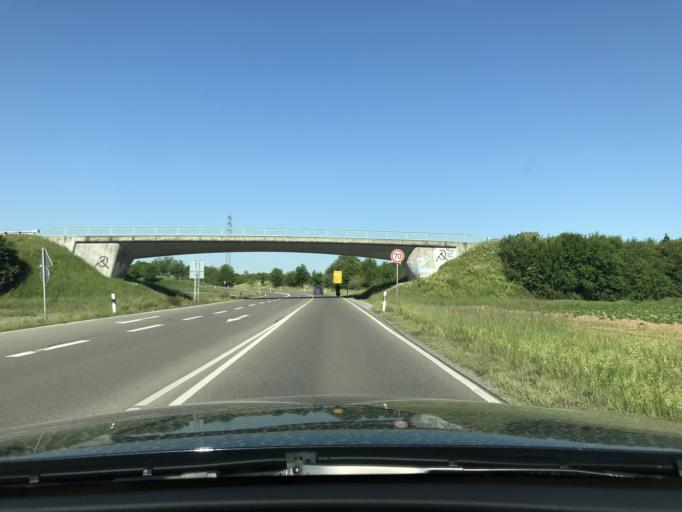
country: DE
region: Baden-Wuerttemberg
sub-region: Regierungsbezirk Stuttgart
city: Waiblingen
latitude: 48.8366
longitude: 9.2970
